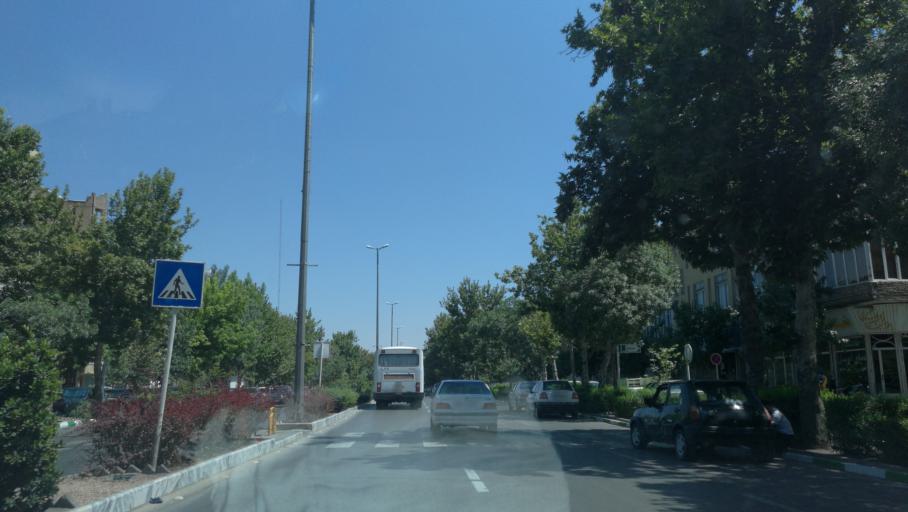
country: IR
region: Razavi Khorasan
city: Mashhad
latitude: 36.2732
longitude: 59.5935
